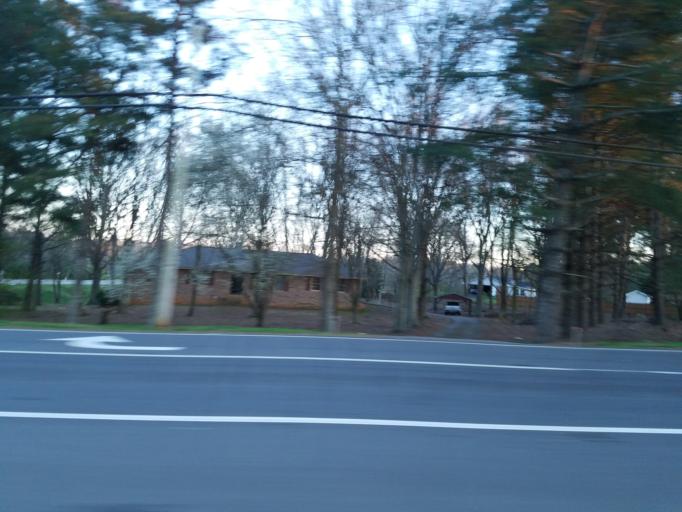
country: US
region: Georgia
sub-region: Forsyth County
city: Cumming
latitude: 34.2681
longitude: -84.0566
